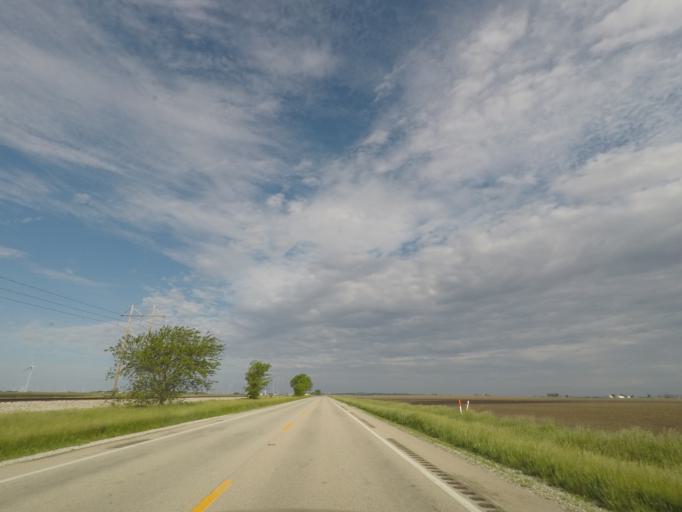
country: US
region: Illinois
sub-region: Logan County
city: Mount Pulaski
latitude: 39.9886
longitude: -89.2338
